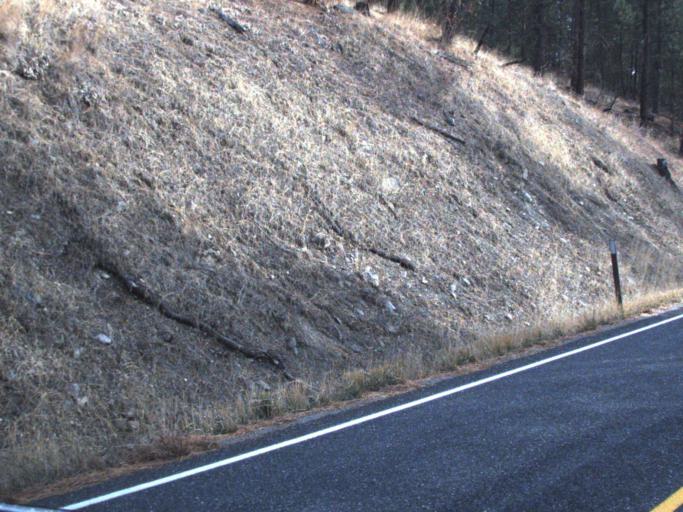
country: US
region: Washington
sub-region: Stevens County
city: Kettle Falls
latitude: 48.3105
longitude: -118.1487
